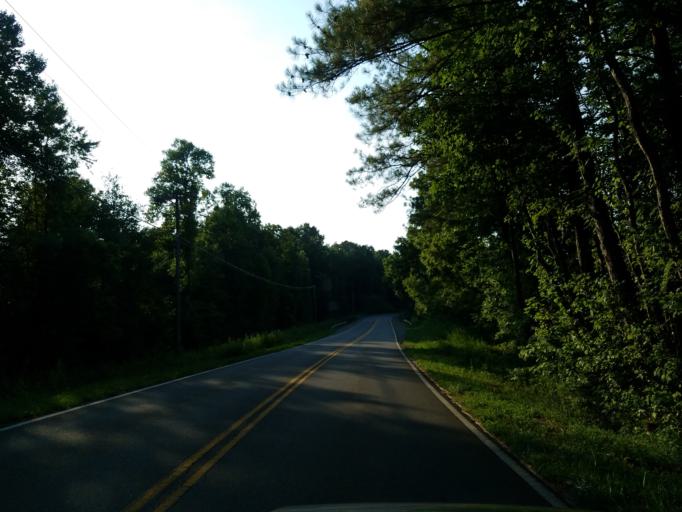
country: US
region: Georgia
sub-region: Pickens County
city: Jasper
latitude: 34.5411
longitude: -84.5405
